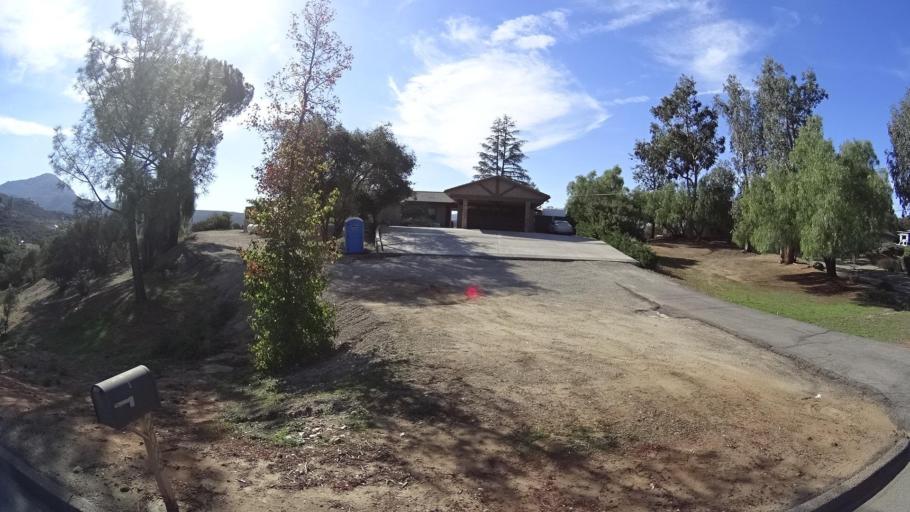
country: US
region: California
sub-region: San Diego County
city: Alpine
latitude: 32.8220
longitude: -116.7439
